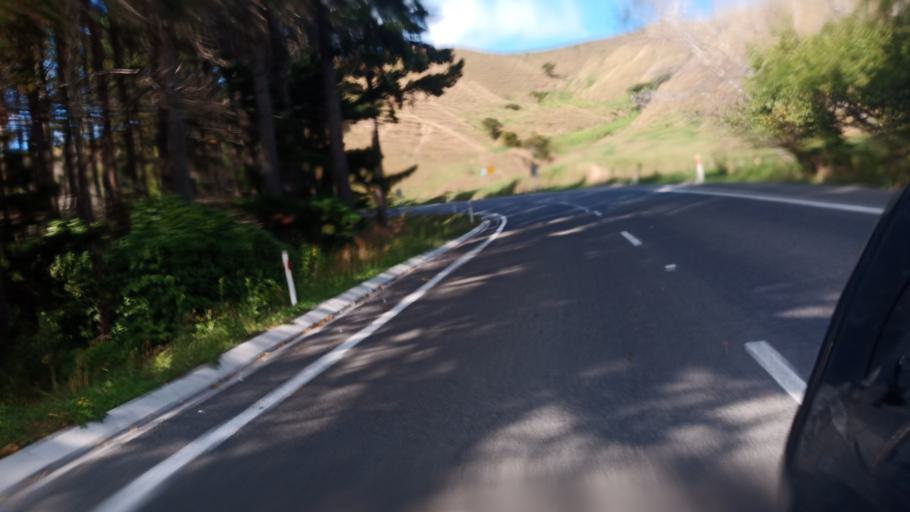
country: NZ
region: Gisborne
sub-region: Gisborne District
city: Gisborne
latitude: -38.4707
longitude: 178.2570
